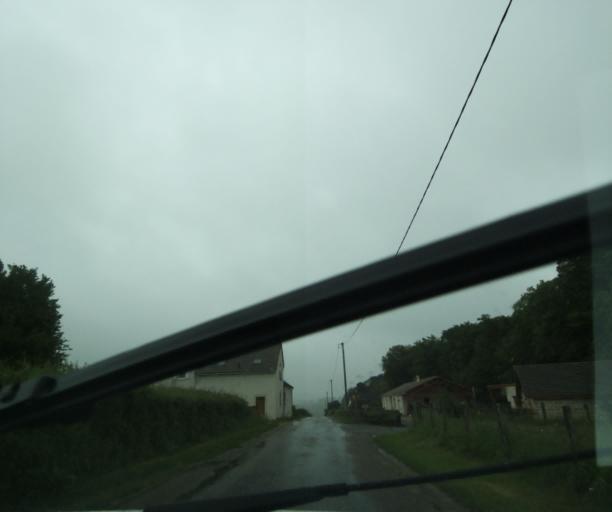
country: FR
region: Bourgogne
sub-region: Departement de Saone-et-Loire
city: Charolles
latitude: 46.4179
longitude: 4.2689
